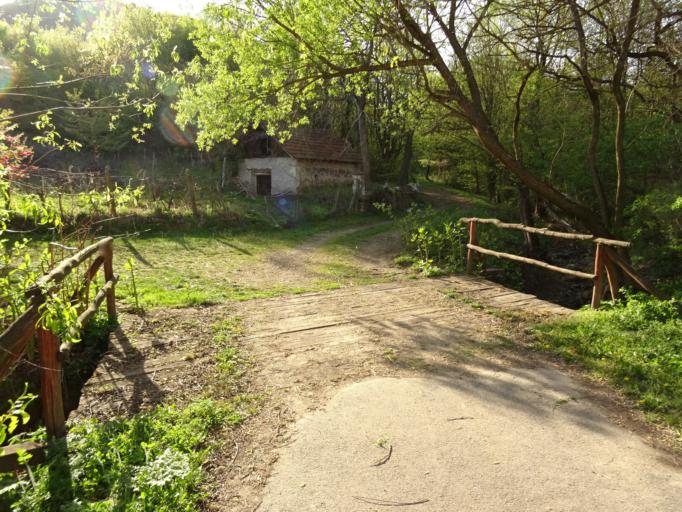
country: HU
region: Borsod-Abauj-Zemplen
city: Gonc
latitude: 48.5460
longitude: 21.4855
